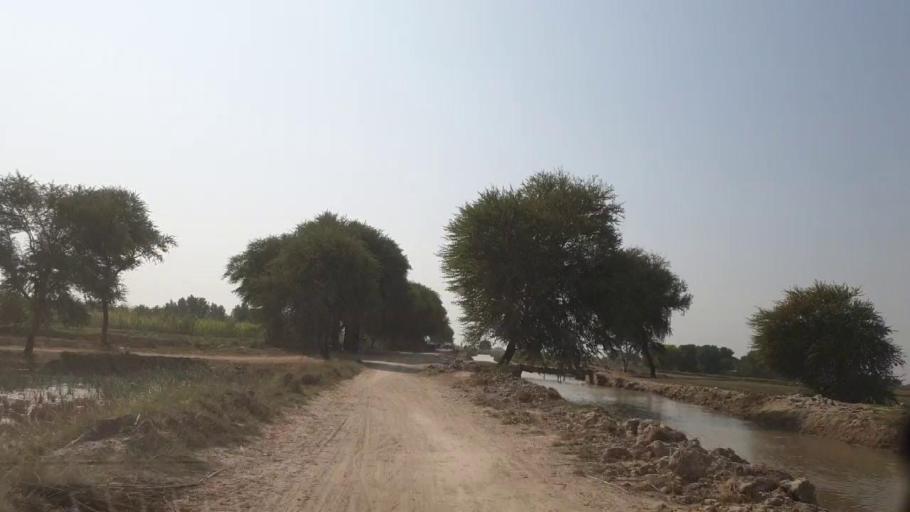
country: PK
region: Sindh
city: Bulri
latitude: 24.9552
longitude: 68.3846
